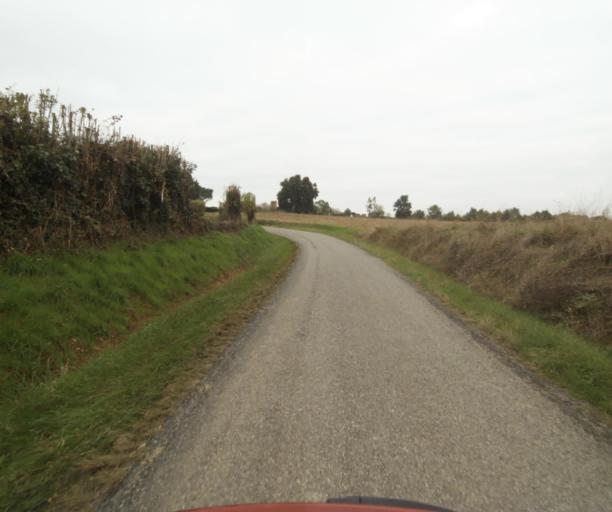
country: FR
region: Midi-Pyrenees
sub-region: Departement du Tarn-et-Garonne
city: Verdun-sur-Garonne
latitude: 43.8041
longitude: 1.2316
